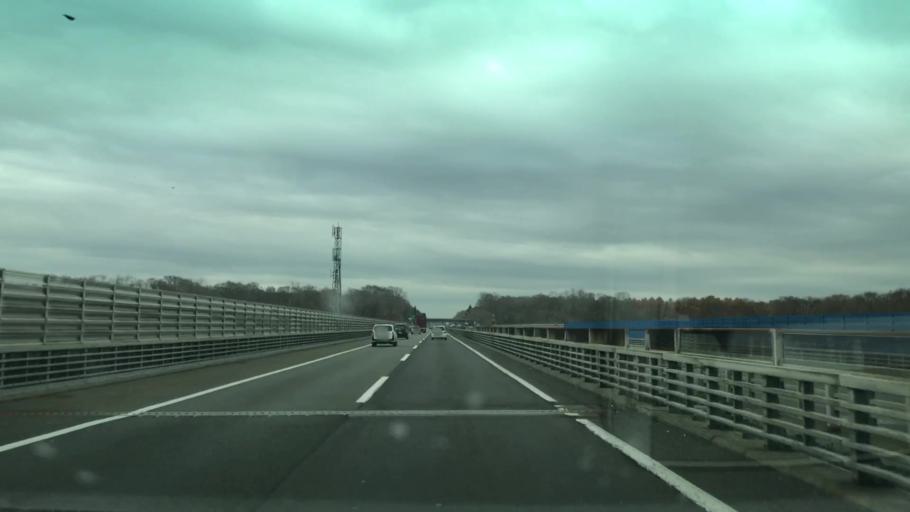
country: JP
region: Hokkaido
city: Chitose
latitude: 42.8182
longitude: 141.6183
